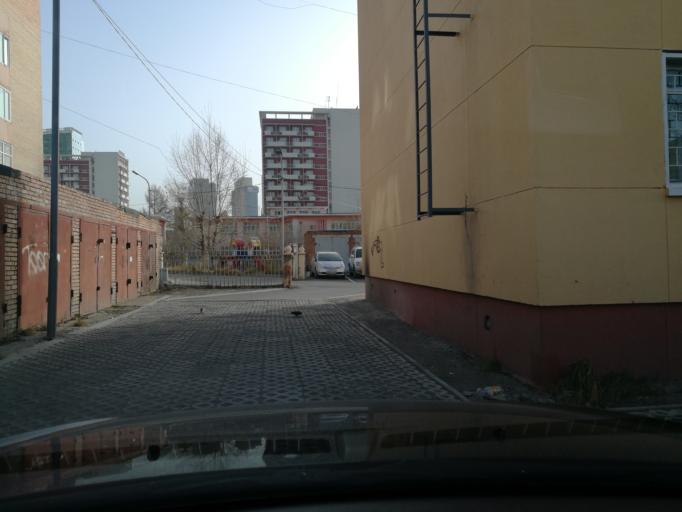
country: MN
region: Ulaanbaatar
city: Ulaanbaatar
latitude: 47.9118
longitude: 106.9111
